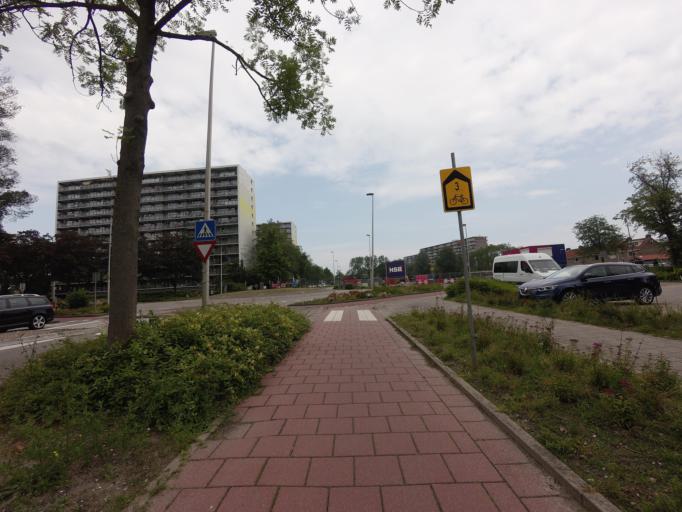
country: NL
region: North Holland
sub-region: Gemeente Purmerend
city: Purmerend
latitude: 52.5065
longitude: 4.9667
